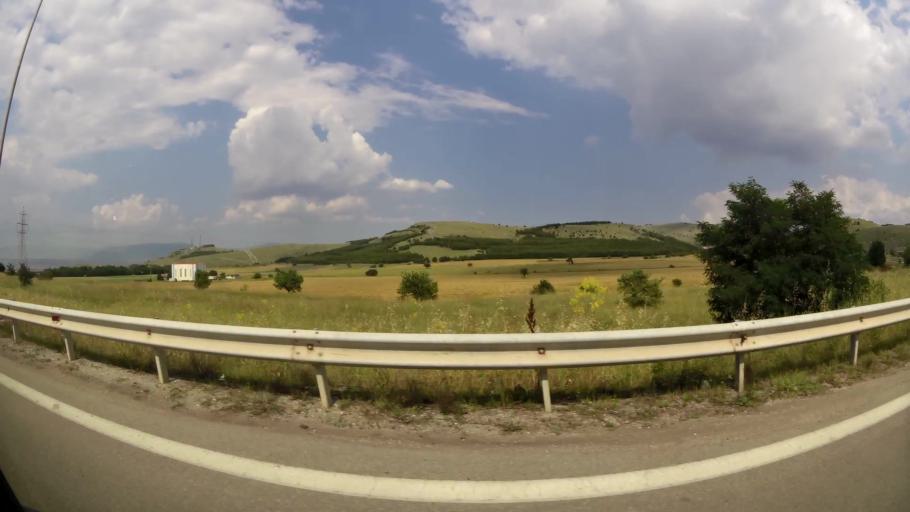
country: GR
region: West Macedonia
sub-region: Nomos Kozanis
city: Koila
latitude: 40.3452
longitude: 21.8061
